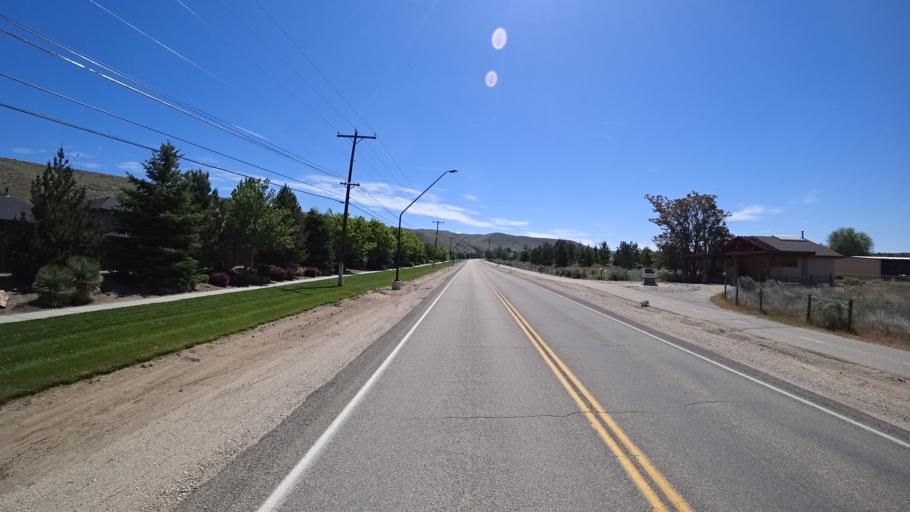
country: US
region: Idaho
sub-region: Ada County
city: Boise
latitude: 43.5640
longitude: -116.1108
